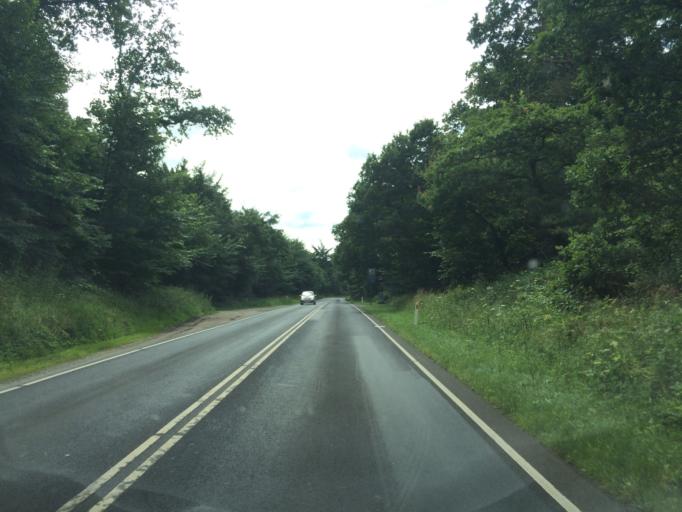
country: DK
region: South Denmark
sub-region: Faaborg-Midtfyn Kommune
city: Faaborg
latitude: 55.1281
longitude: 10.2567
